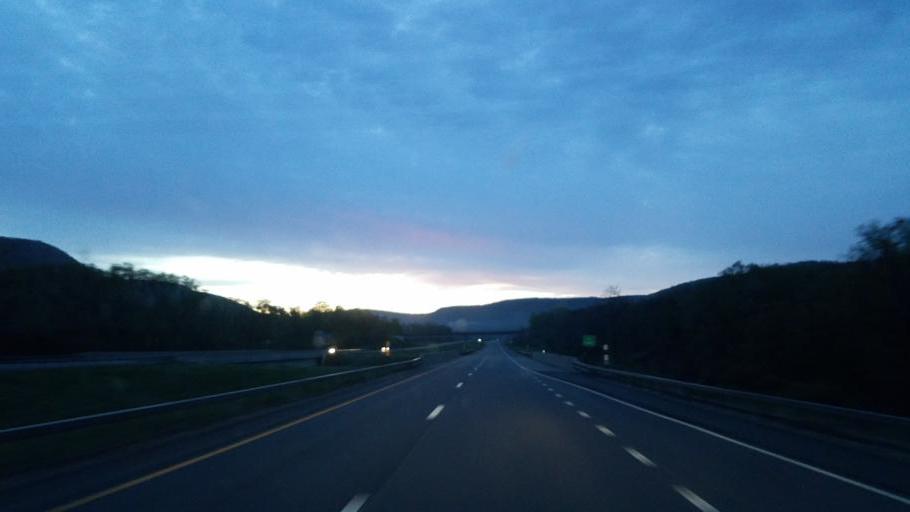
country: US
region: New York
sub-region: Cattaraugus County
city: Weston Mills
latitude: 42.1766
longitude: -78.3769
